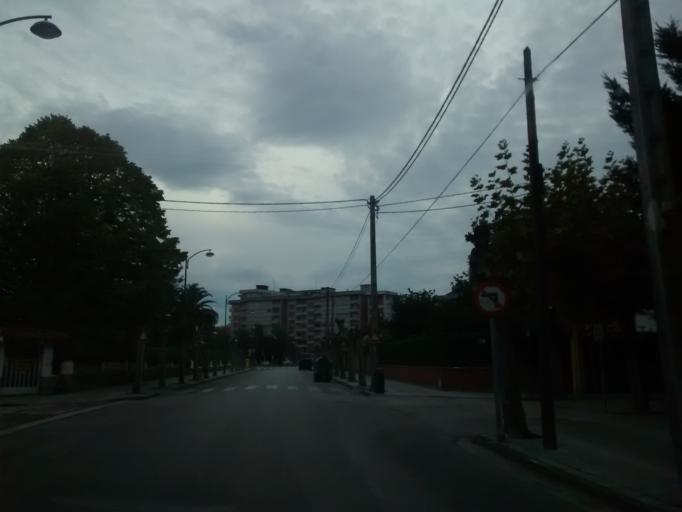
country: ES
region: Cantabria
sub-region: Provincia de Cantabria
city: Laredo
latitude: 43.4093
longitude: -3.4269
